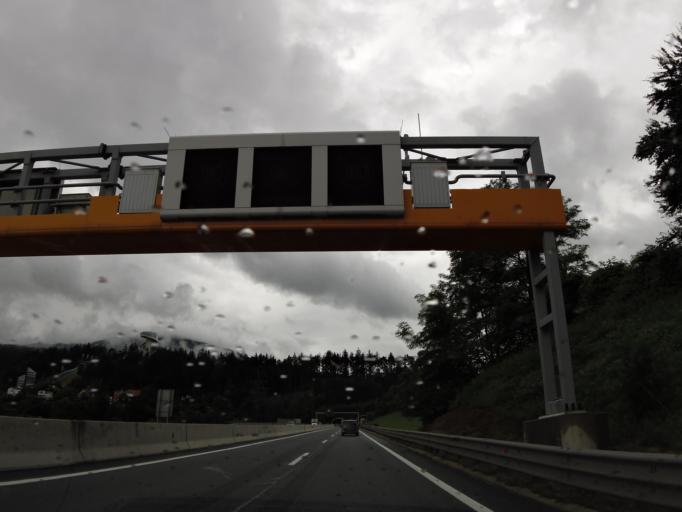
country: AT
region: Tyrol
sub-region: Innsbruck Stadt
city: Innsbruck
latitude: 47.2512
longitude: 11.3925
